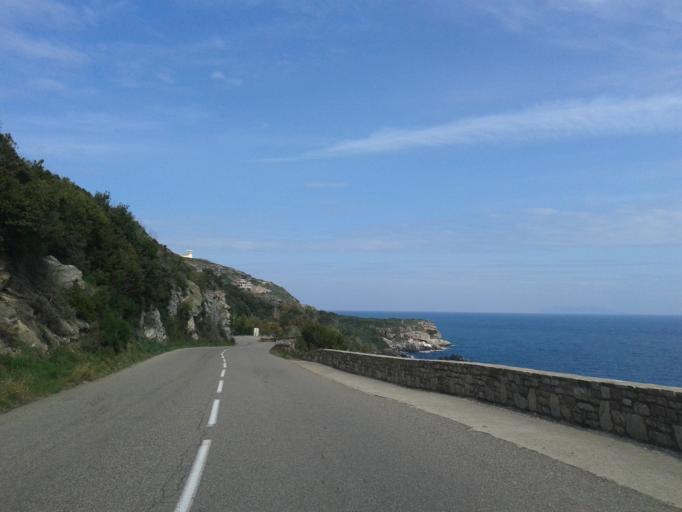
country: FR
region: Corsica
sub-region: Departement de la Haute-Corse
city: Brando
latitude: 42.7887
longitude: 9.4860
